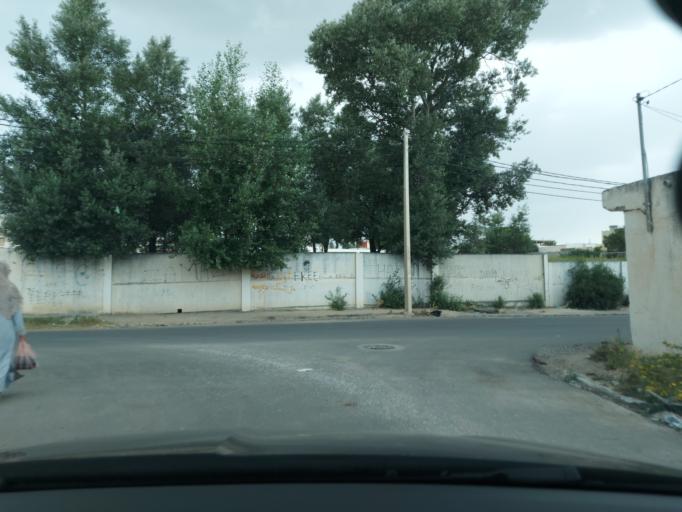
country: TN
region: Silyanah
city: Maktar
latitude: 35.8539
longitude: 9.1972
